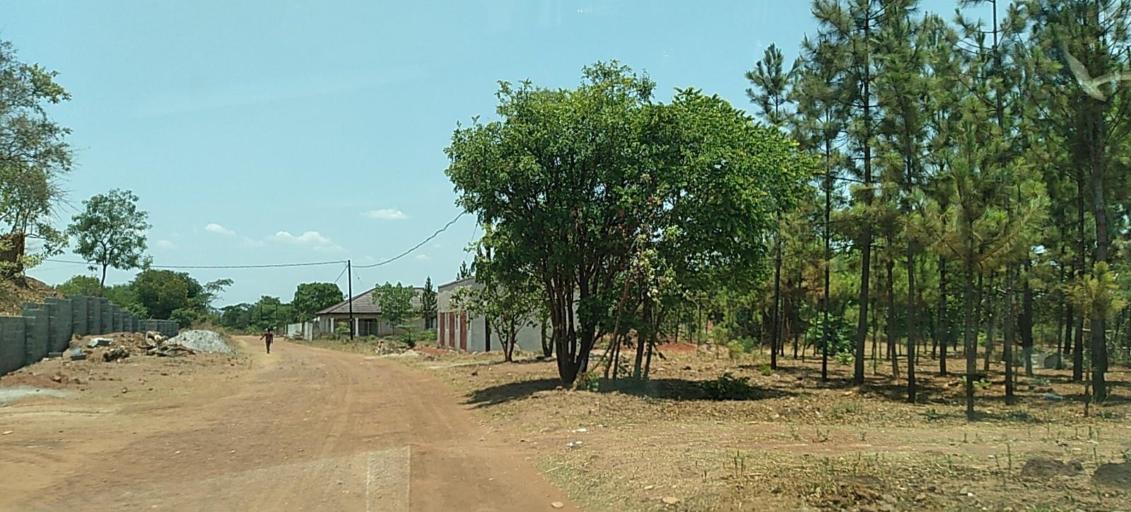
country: ZM
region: Copperbelt
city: Luanshya
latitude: -13.1048
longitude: 28.4048
